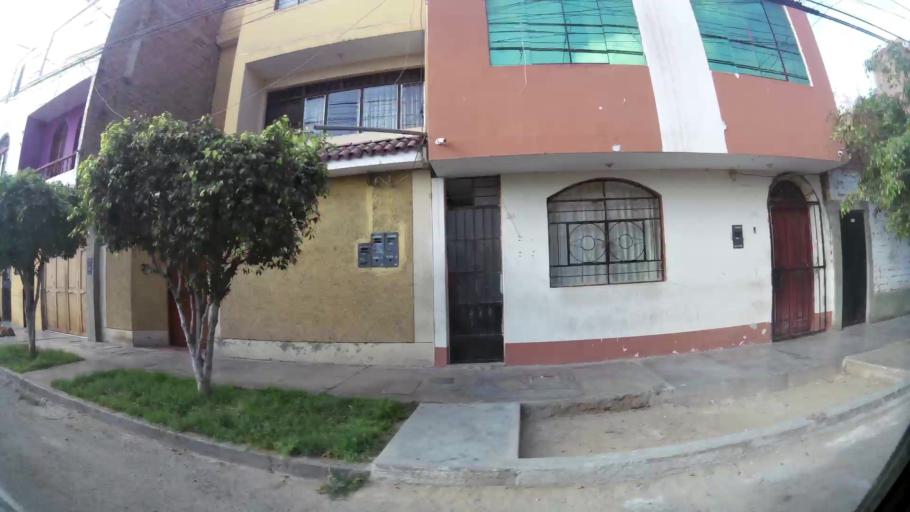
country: PE
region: La Libertad
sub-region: Provincia de Trujillo
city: Trujillo
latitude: -8.1042
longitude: -79.0138
